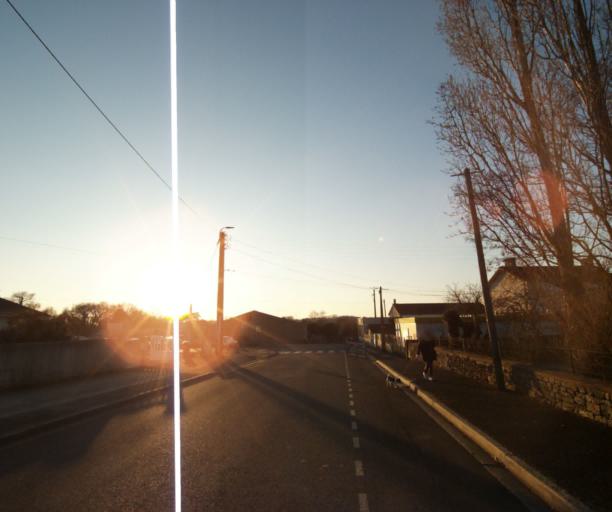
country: FR
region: Poitou-Charentes
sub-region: Departement des Deux-Sevres
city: Niort
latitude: 46.3563
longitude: -0.4521
